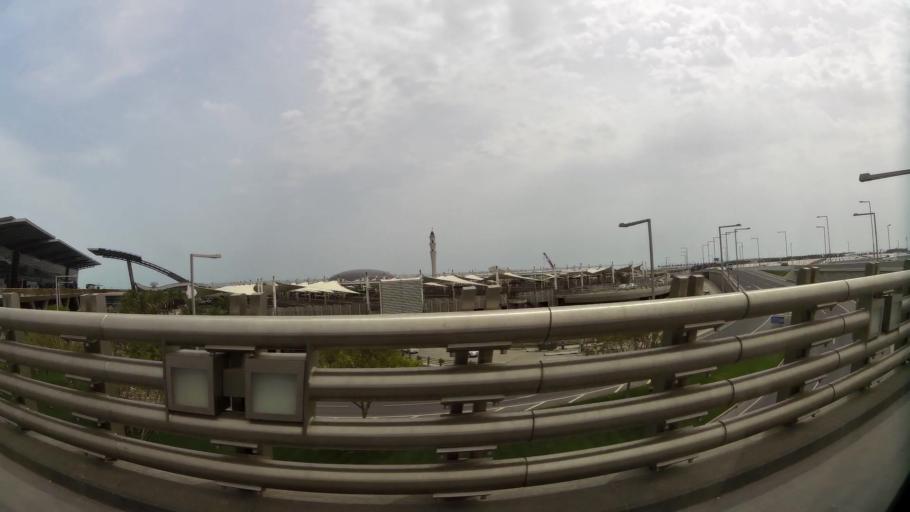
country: QA
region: Al Wakrah
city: Al Wakrah
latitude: 25.2583
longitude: 51.6118
